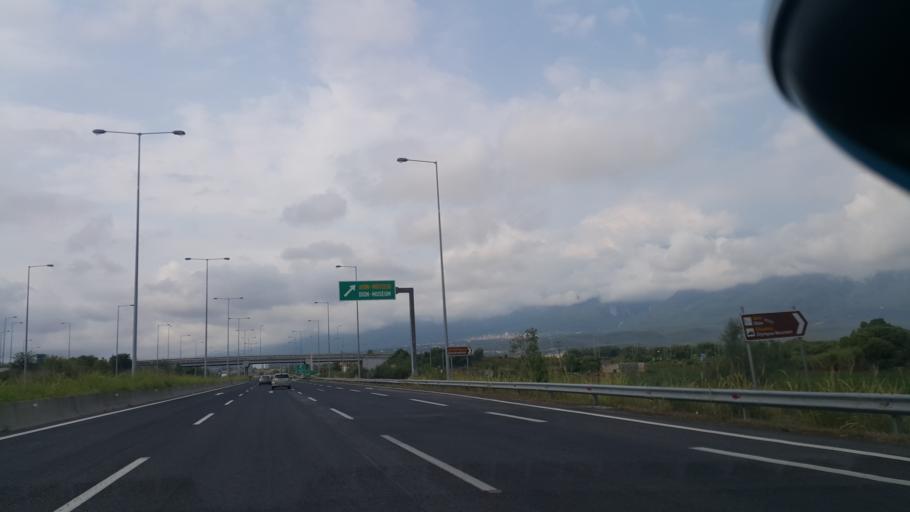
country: GR
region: Central Macedonia
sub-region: Nomos Pierias
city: Dion
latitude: 40.1536
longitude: 22.5422
